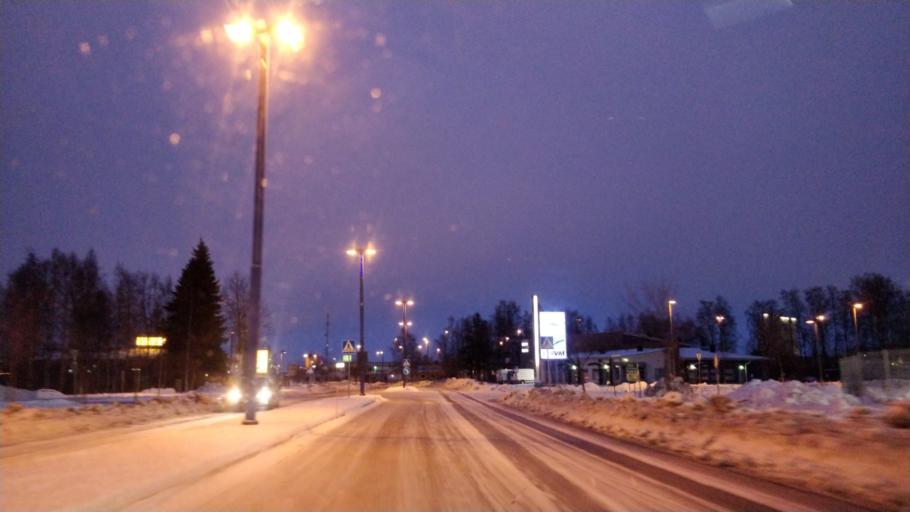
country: FI
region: Lapland
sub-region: Kemi-Tornio
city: Kemi
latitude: 65.7416
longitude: 24.5768
